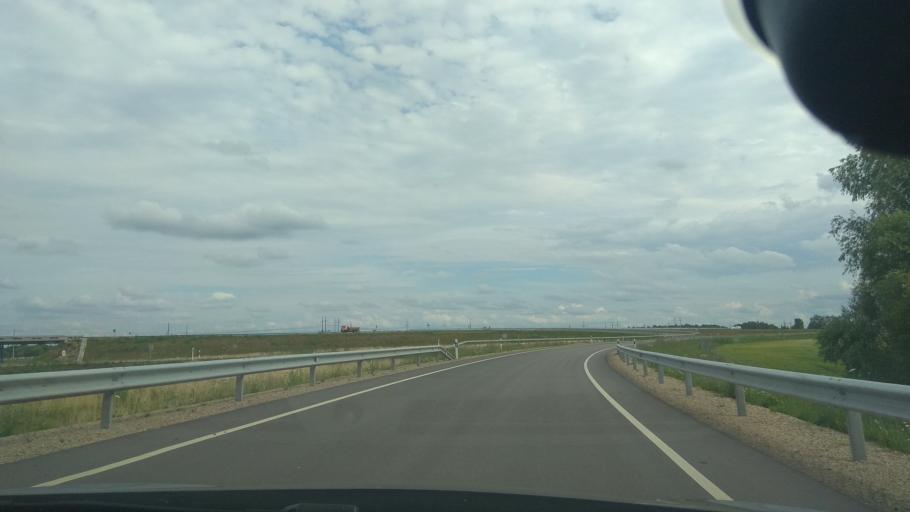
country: LT
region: Panevezys
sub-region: Panevezys City
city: Panevezys
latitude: 55.7332
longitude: 24.2720
